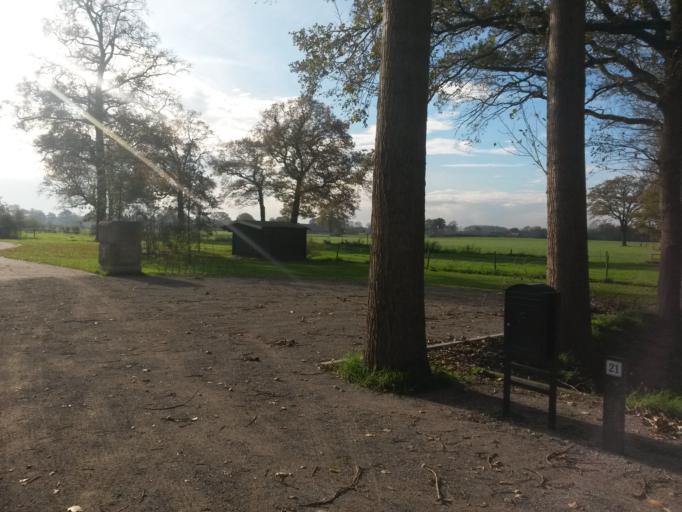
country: NL
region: Overijssel
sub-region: Gemeente Wierden
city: Wierden
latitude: 52.3287
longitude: 6.5805
